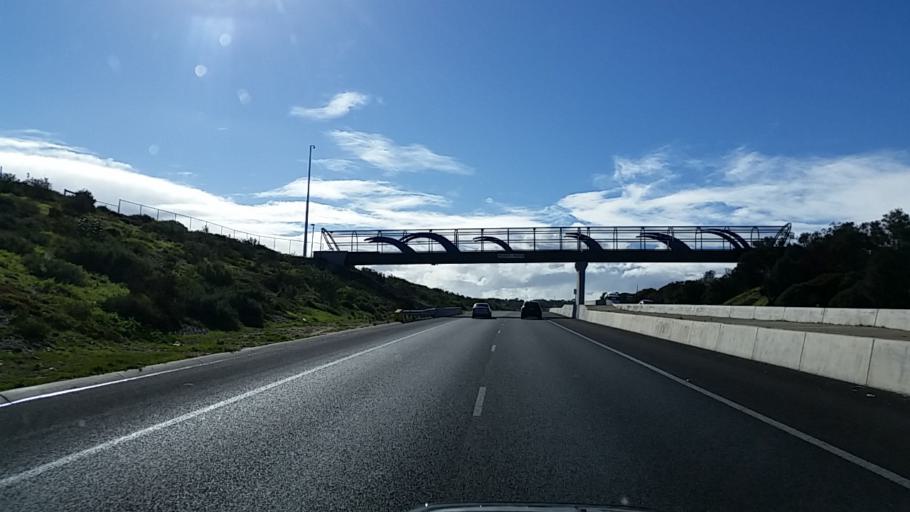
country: AU
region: South Australia
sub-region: Onkaparinga
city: Noarlunga Downs
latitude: -35.1584
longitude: 138.5065
